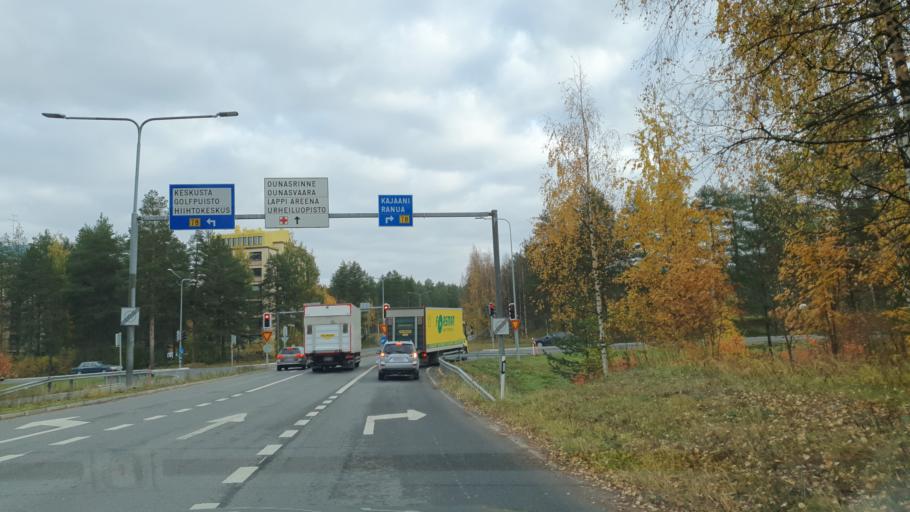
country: FI
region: Lapland
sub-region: Rovaniemi
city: Rovaniemi
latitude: 66.4972
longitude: 25.7553
